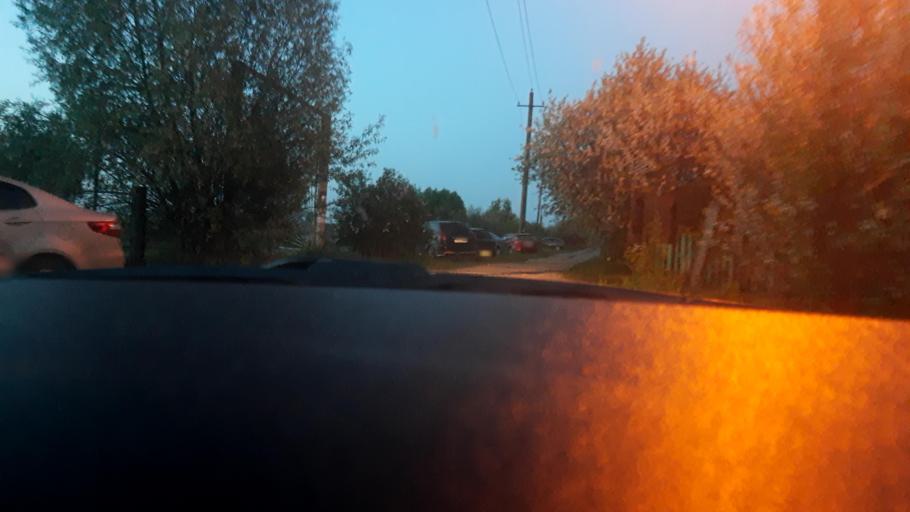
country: RU
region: Bashkortostan
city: Iglino
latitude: 54.7613
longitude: 56.3318
